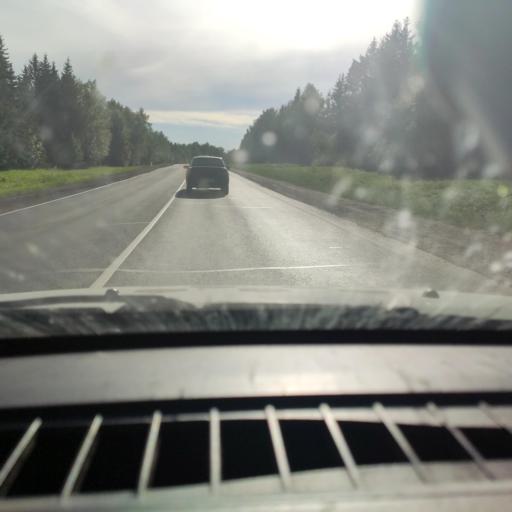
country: RU
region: Kirov
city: Vakhrushi
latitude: 58.6782
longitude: 49.9890
